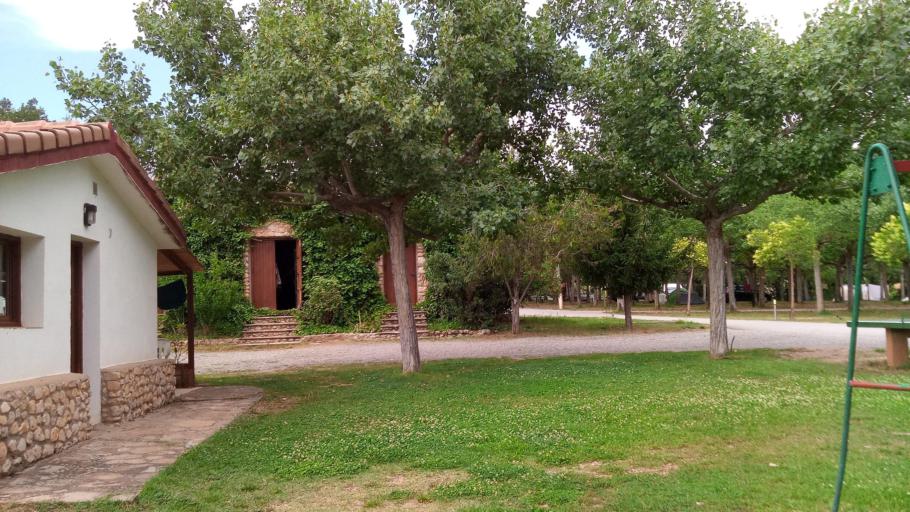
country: ES
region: Aragon
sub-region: Provincia de Huesca
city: Castigaleu
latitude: 42.3077
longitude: 0.5452
